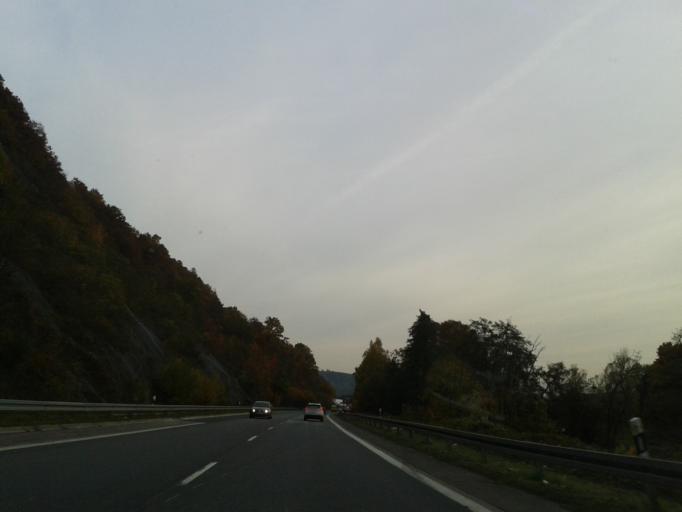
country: DE
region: Hesse
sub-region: Regierungsbezirk Giessen
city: Sinn
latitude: 50.6627
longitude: 8.3249
